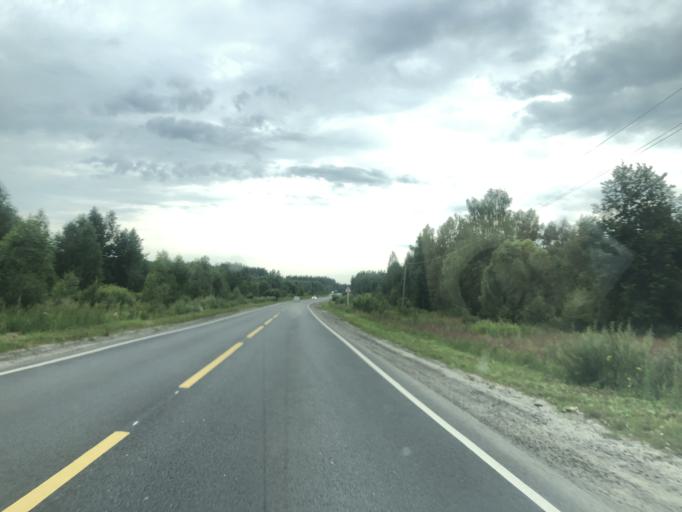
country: RU
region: Ivanovo
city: Pestyaki
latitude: 56.7037
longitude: 42.7415
